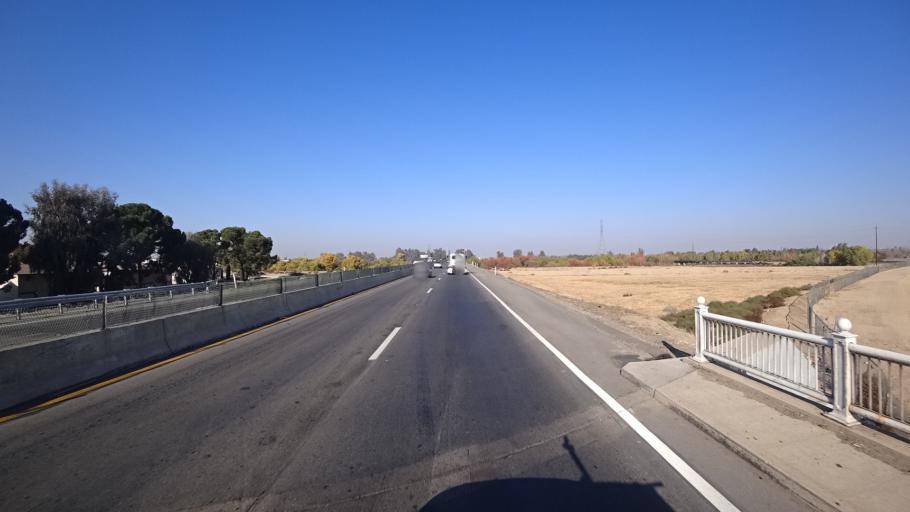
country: US
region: California
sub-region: Kern County
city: Bakersfield
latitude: 35.3932
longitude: -119.0277
